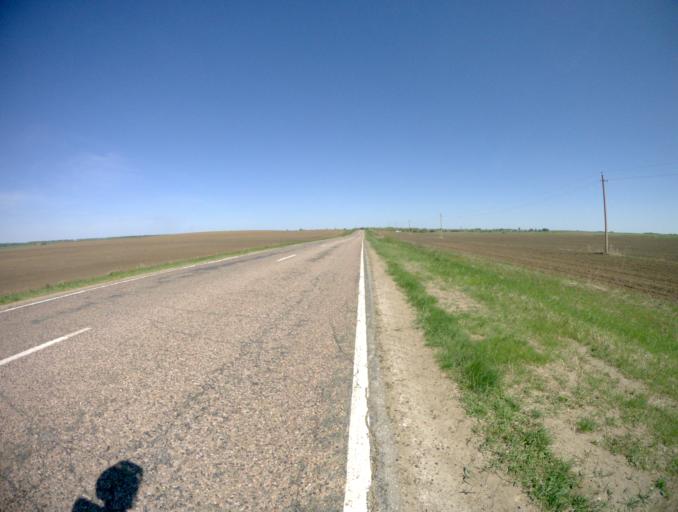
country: RU
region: Vladimir
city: Suzdal'
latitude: 56.3693
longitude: 40.4083
